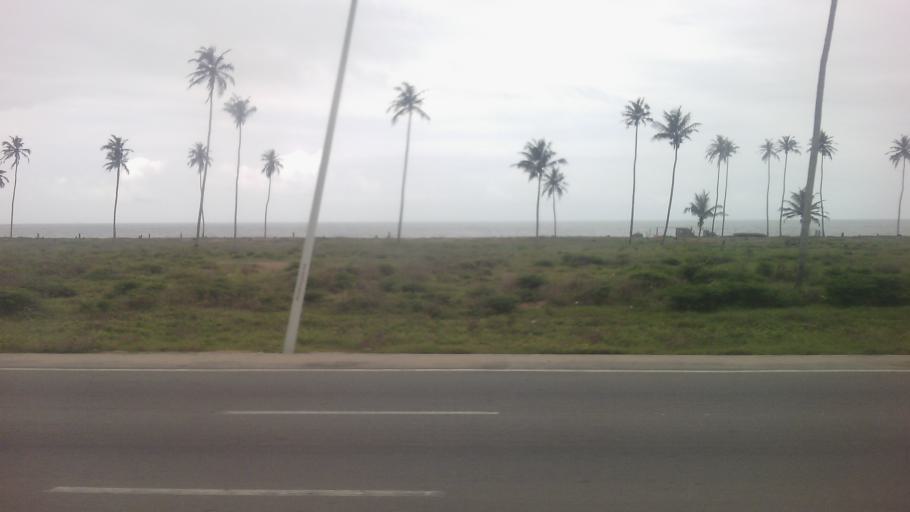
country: CI
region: Lagunes
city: Bingerville
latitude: 5.2370
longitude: -3.8811
